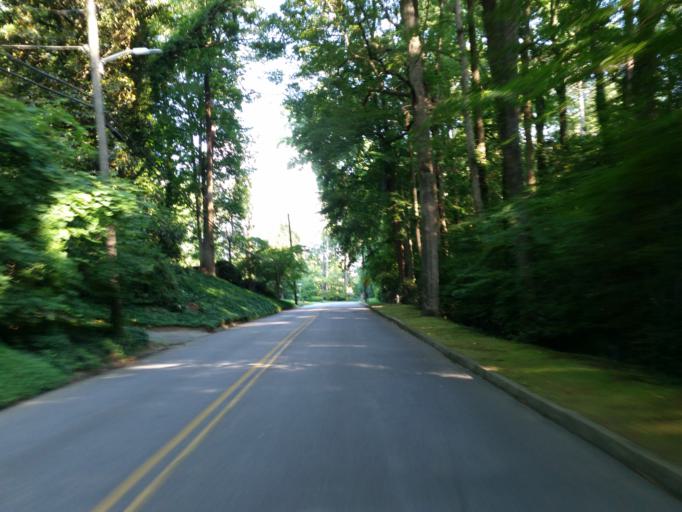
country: US
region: Georgia
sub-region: Cobb County
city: Vinings
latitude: 33.8581
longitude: -84.4222
